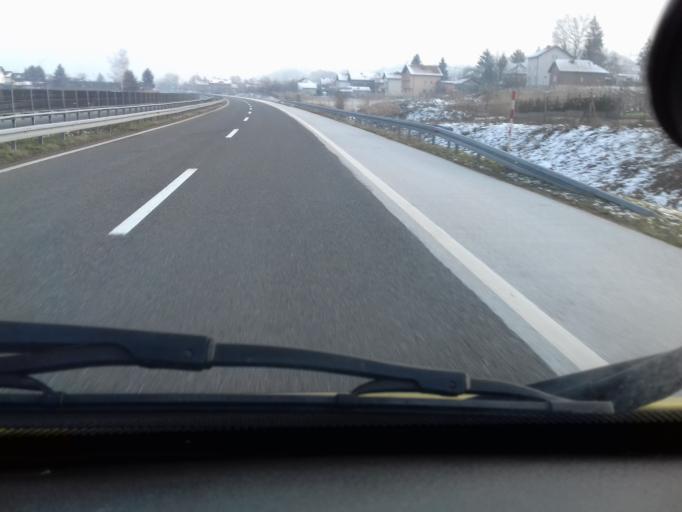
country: BA
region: Federation of Bosnia and Herzegovina
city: Gornje Mostre
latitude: 44.0089
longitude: 18.1449
